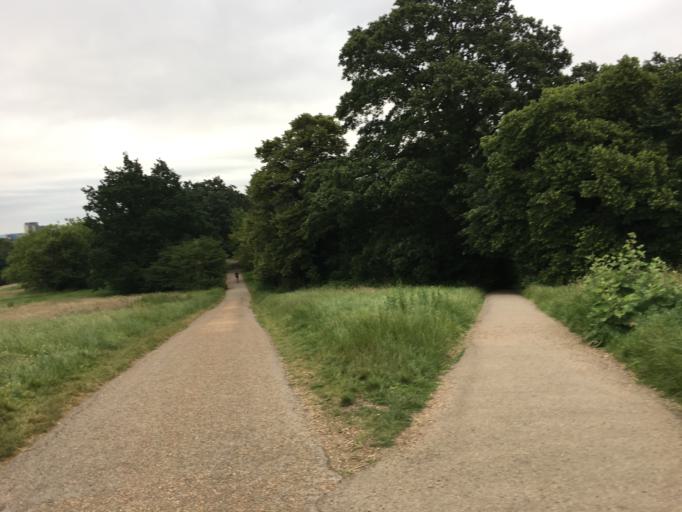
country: GB
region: England
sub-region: Greater London
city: Belsize Park
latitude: 51.5597
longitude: -0.1588
